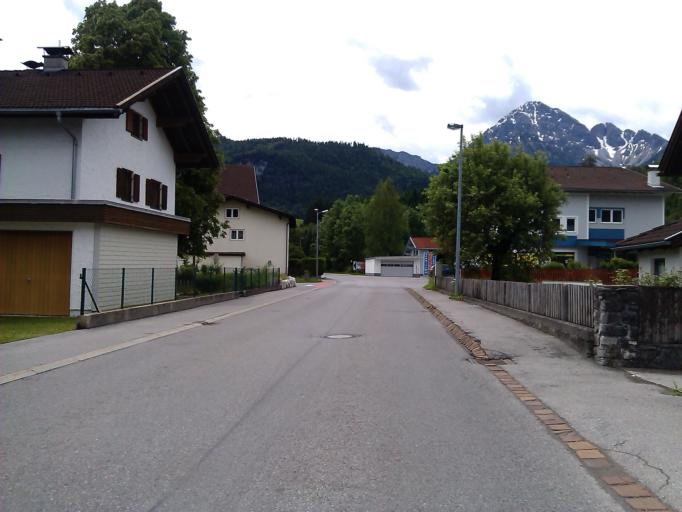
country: AT
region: Tyrol
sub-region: Politischer Bezirk Reutte
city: Reutte
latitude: 47.4803
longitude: 10.7208
